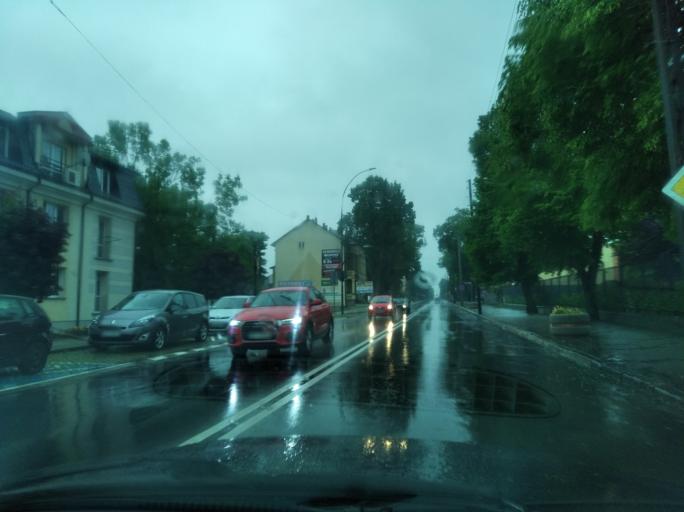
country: PL
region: Subcarpathian Voivodeship
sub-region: Powiat jasielski
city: Jaslo
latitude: 49.7423
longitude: 21.4687
